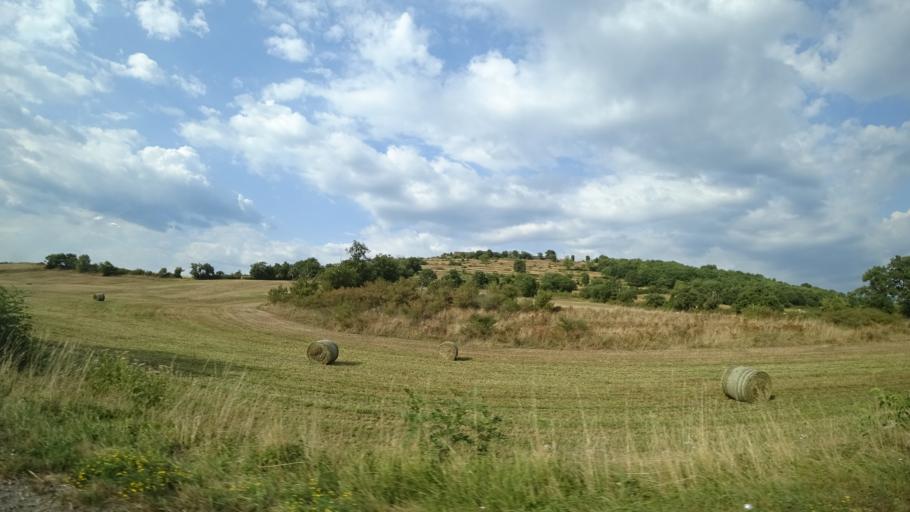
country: FR
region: Midi-Pyrenees
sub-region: Departement de l'Aveyron
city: Saint-Christophe-Vallon
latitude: 44.4873
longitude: 2.3943
